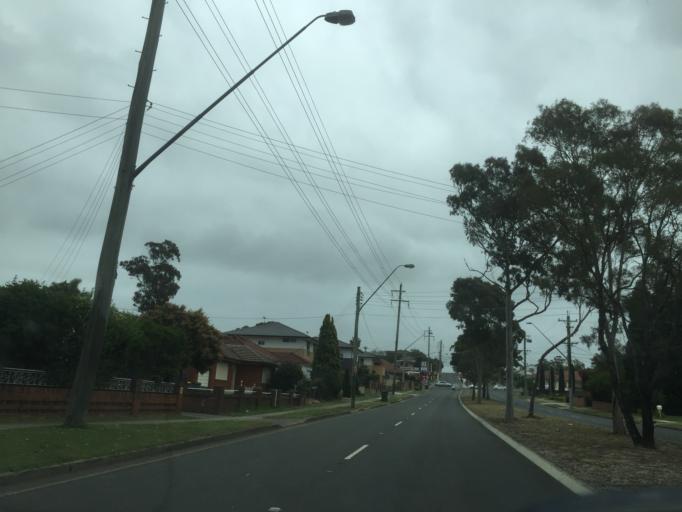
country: AU
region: New South Wales
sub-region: Blacktown
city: Blacktown
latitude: -33.7762
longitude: 150.8972
